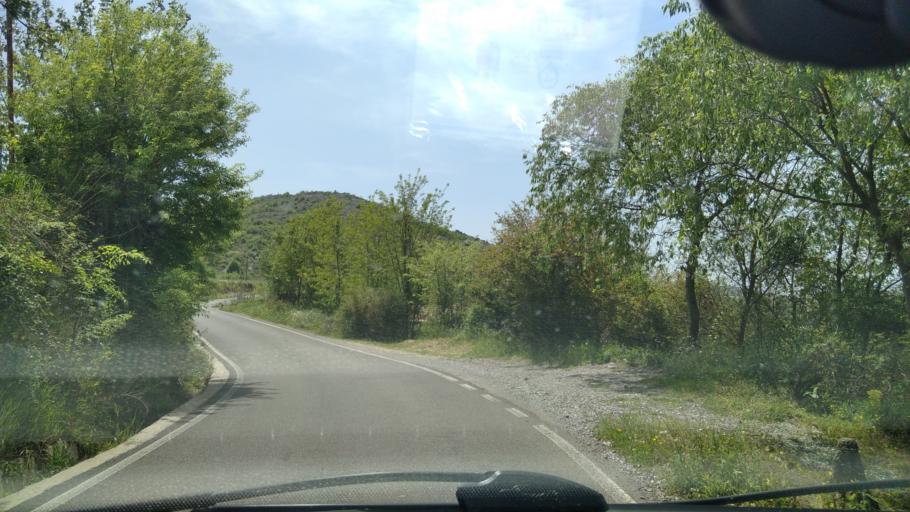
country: AL
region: Shkoder
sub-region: Rrethi i Malesia e Madhe
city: Gruemire
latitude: 42.1197
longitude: 19.5794
